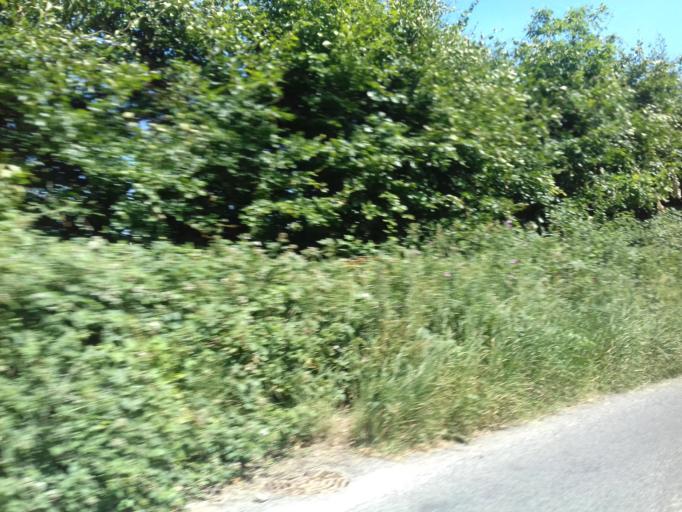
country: IE
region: Leinster
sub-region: An Mhi
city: Ashbourne
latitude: 53.5262
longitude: -6.2975
